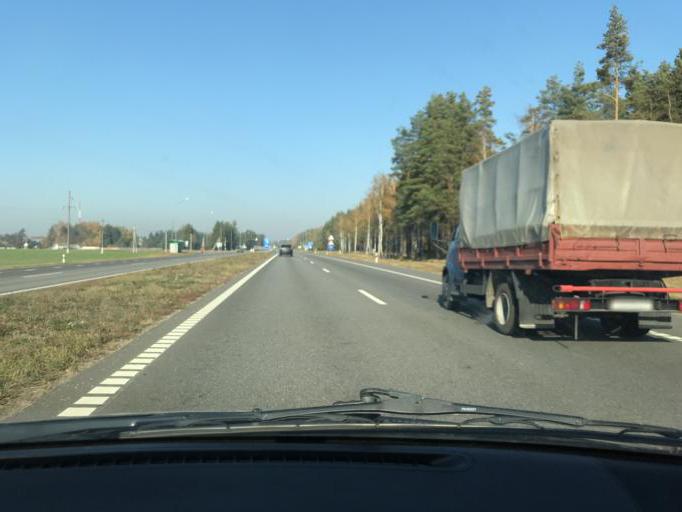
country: BY
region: Minsk
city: Slutsk
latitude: 53.3223
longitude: 27.5340
